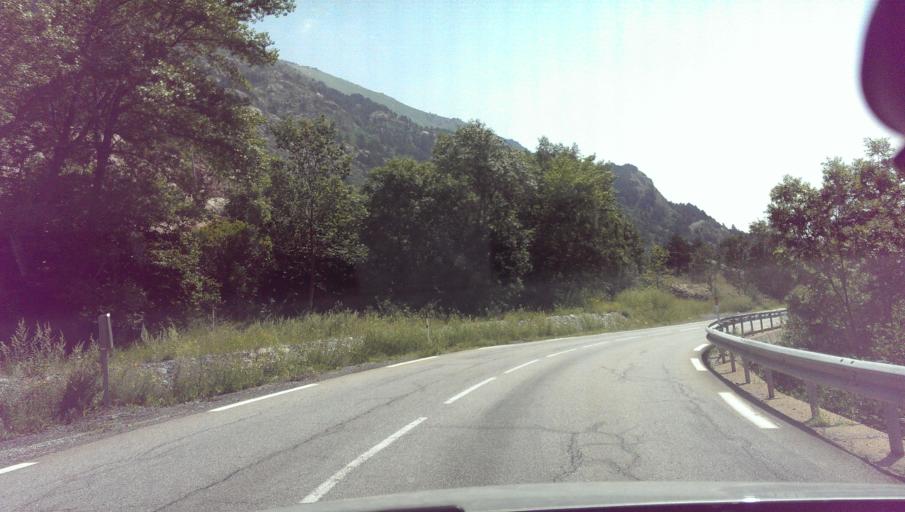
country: ES
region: Catalonia
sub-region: Provincia de Girona
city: Meranges
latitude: 42.5124
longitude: 1.8269
